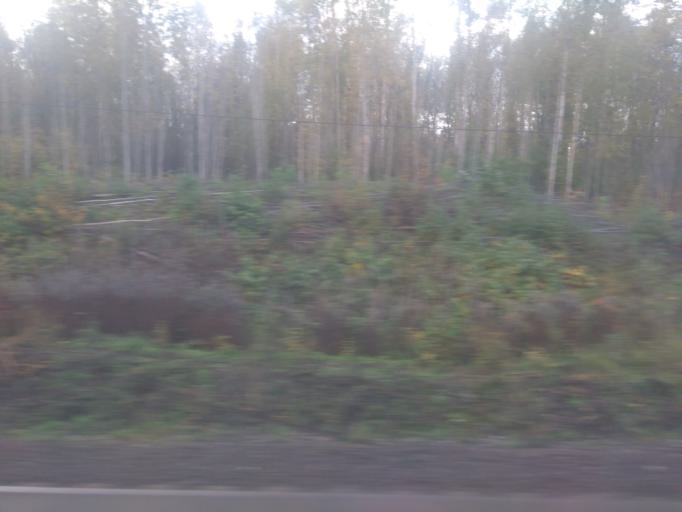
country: RU
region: Udmurtiya
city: Mozhga
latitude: 56.4264
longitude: 52.0492
